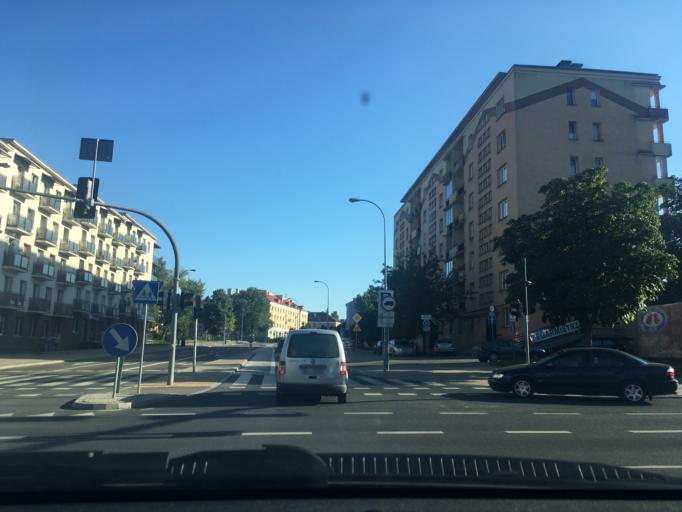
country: PL
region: Podlasie
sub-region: Bialystok
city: Bialystok
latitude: 53.1361
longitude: 23.1519
